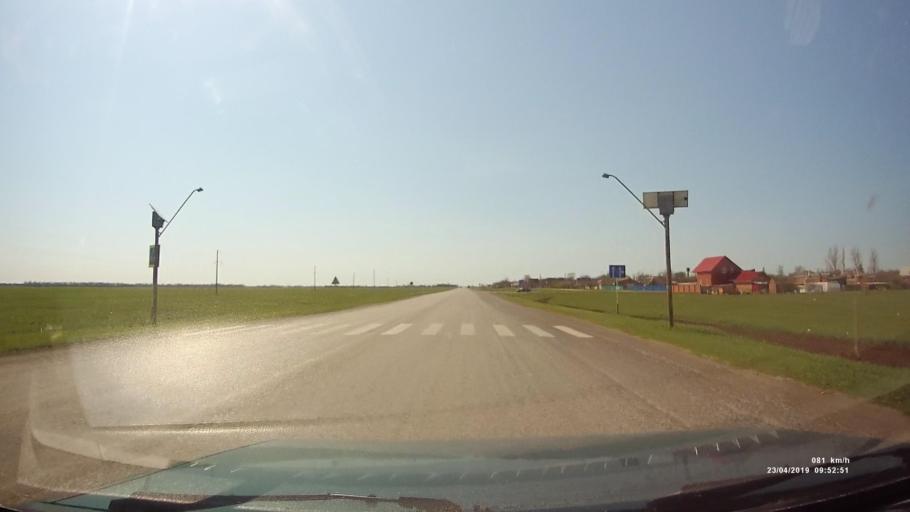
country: RU
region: Rostov
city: Orlovskiy
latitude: 46.8397
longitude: 42.0477
